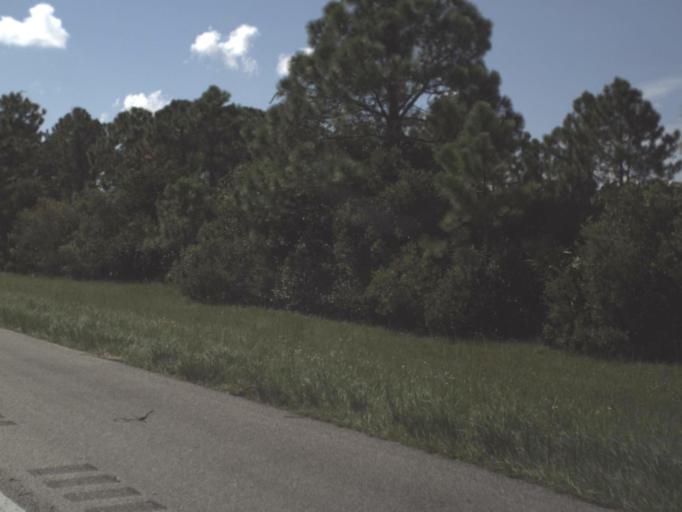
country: US
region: Florida
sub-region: Lee County
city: Suncoast Estates
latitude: 26.7951
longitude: -81.9108
